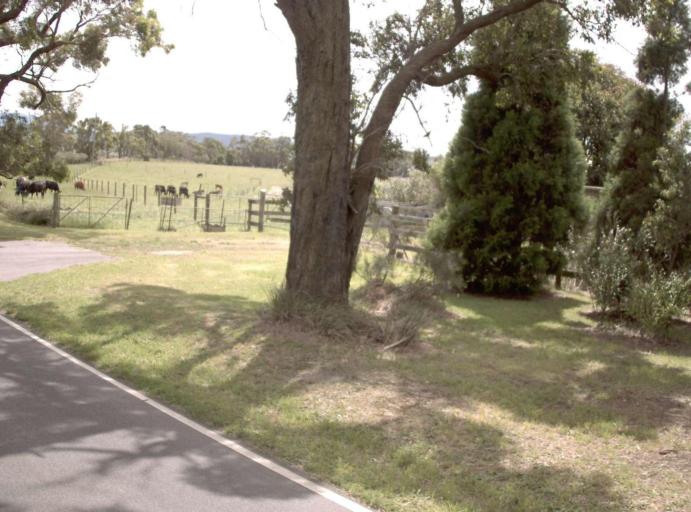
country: AU
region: Victoria
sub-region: Latrobe
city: Moe
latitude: -38.1136
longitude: 146.1504
